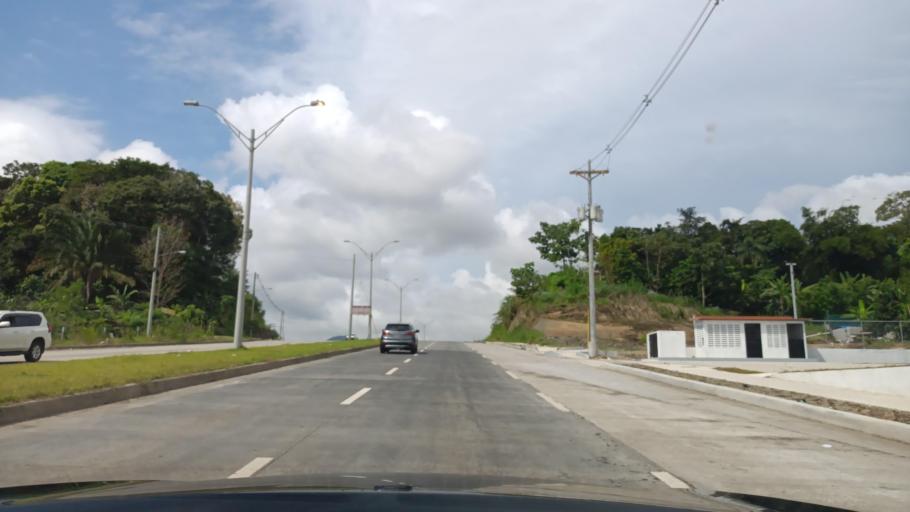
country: PA
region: Panama
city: Las Cumbres
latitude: 9.0987
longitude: -79.5098
